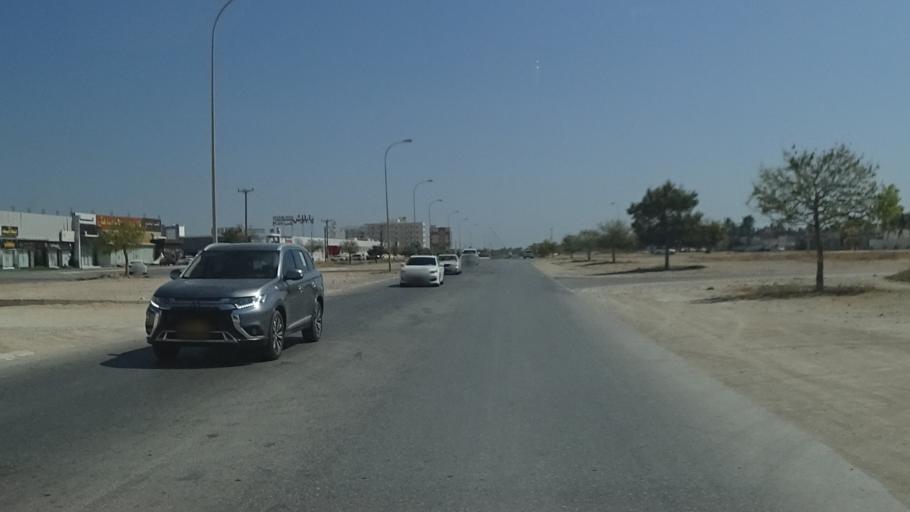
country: OM
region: Zufar
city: Salalah
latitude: 17.0515
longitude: 54.1670
